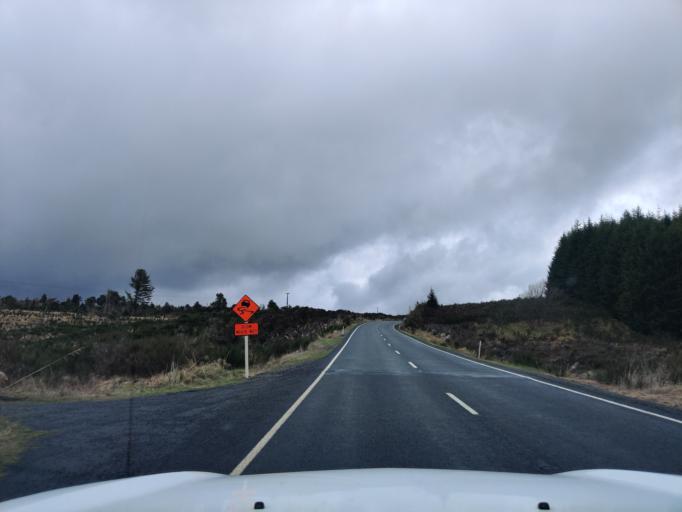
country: NZ
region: Manawatu-Wanganui
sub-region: Ruapehu District
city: Waiouru
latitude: -39.2027
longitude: 175.4022
